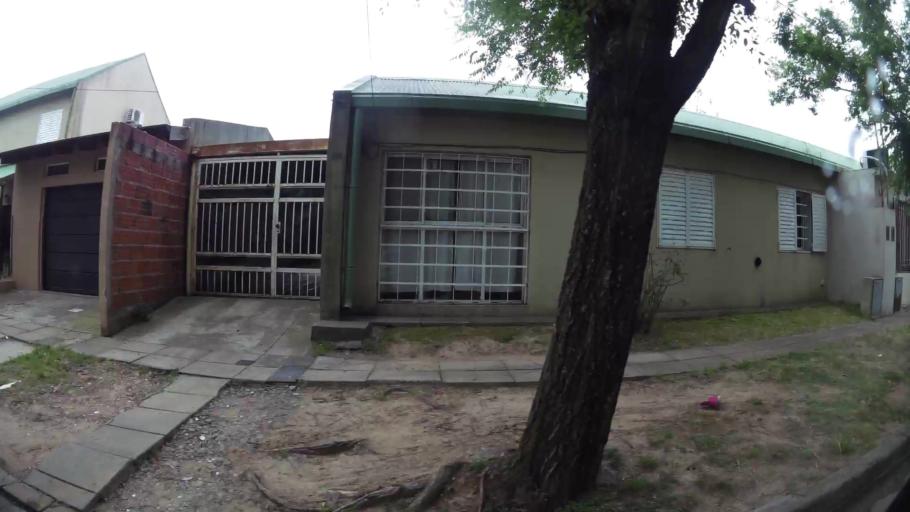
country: AR
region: Buenos Aires
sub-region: Partido de Campana
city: Campana
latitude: -34.2004
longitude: -58.9414
